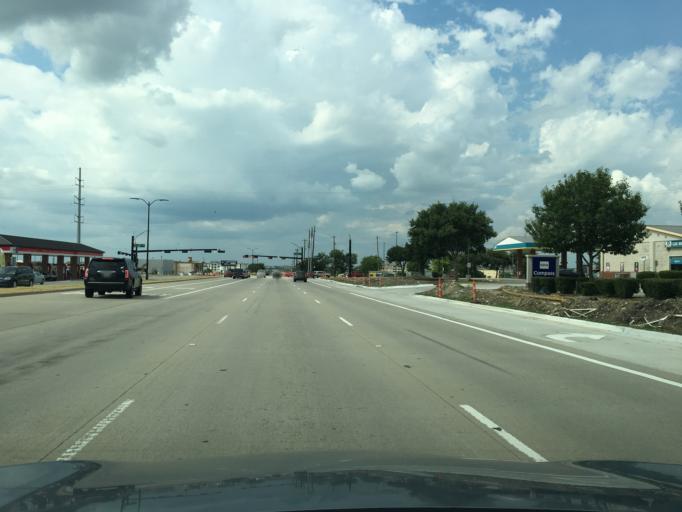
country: US
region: Texas
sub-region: Denton County
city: Little Elm
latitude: 33.1520
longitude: -96.8908
